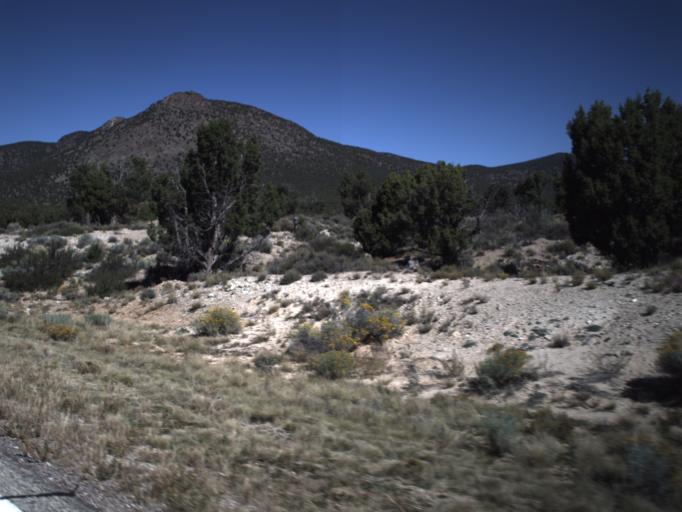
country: US
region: Utah
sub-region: Washington County
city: Enterprise
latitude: 37.6464
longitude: -113.4447
